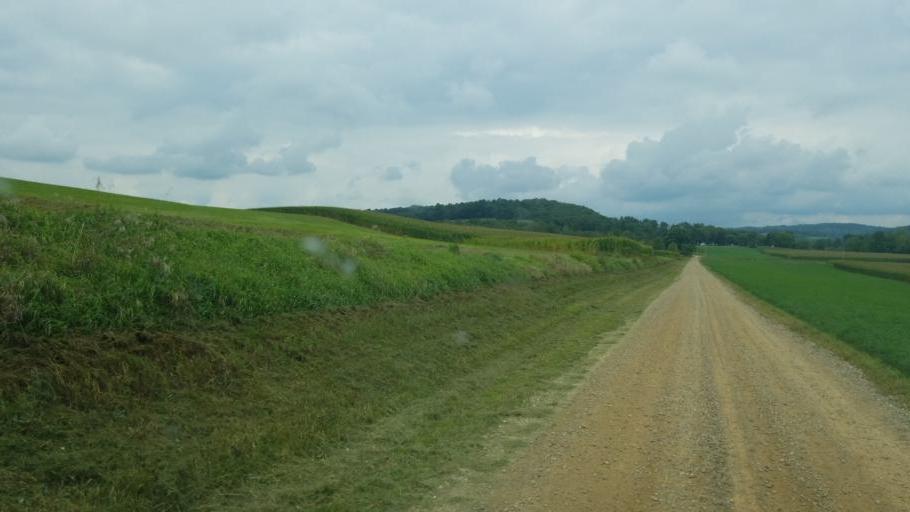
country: US
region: Ohio
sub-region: Knox County
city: Danville
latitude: 40.5240
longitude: -82.3051
